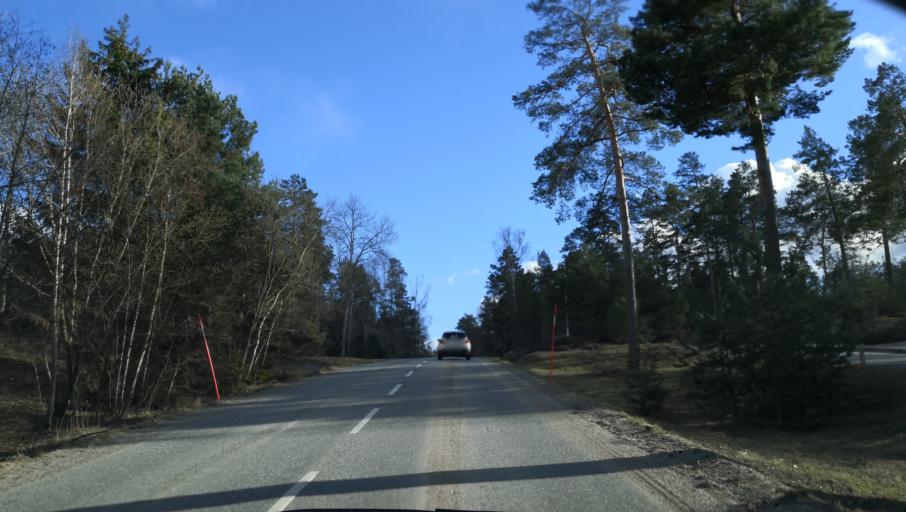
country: SE
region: Stockholm
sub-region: Varmdo Kommun
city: Mortnas
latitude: 59.2851
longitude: 18.4542
